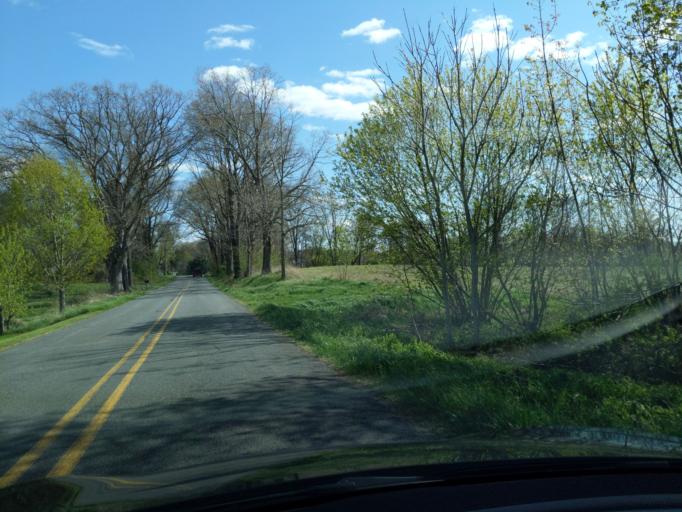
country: US
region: Michigan
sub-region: Jackson County
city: Spring Arbor
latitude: 42.3403
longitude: -84.5220
